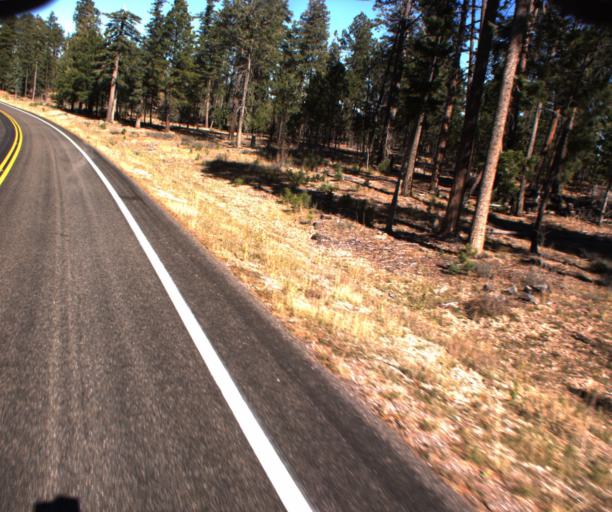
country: US
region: Arizona
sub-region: Coconino County
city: Fredonia
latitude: 36.6282
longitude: -112.1750
